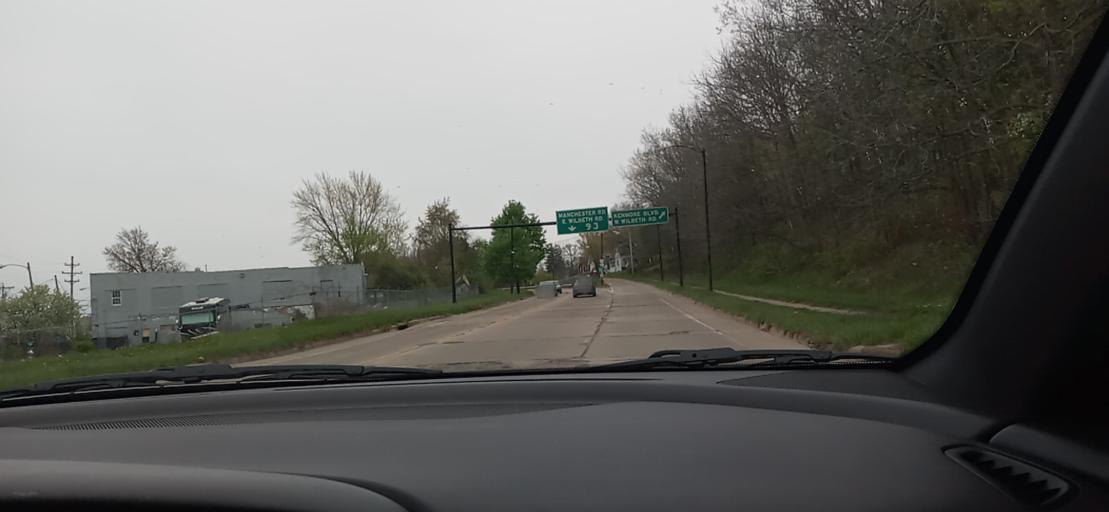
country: US
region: Ohio
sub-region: Summit County
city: Akron
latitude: 41.0482
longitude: -81.5476
